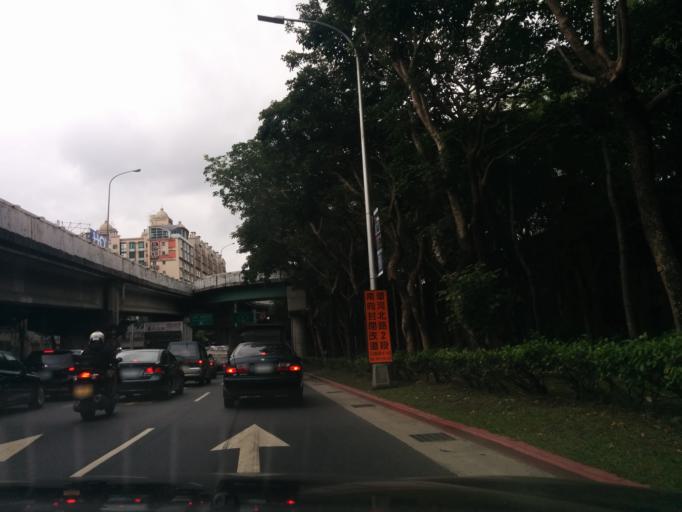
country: TW
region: Taipei
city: Taipei
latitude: 25.0869
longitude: 121.5046
